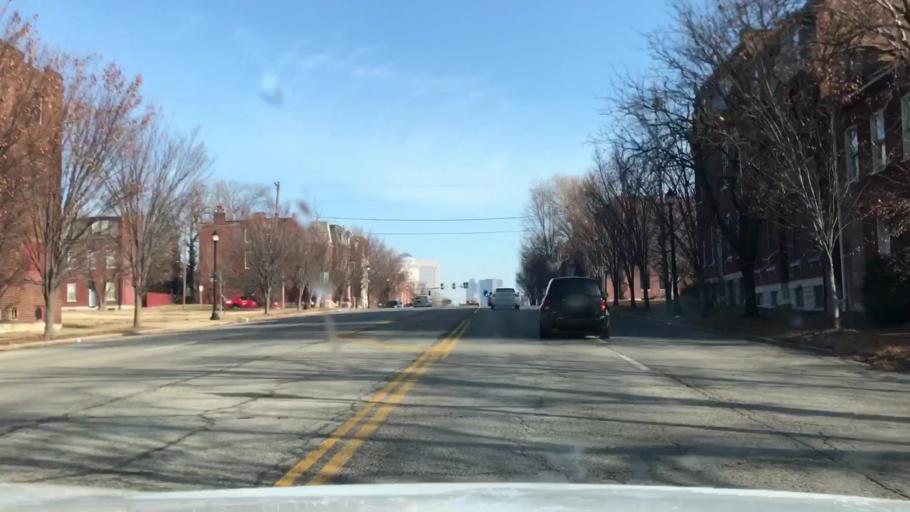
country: US
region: Missouri
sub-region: City of Saint Louis
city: St. Louis
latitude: 38.6113
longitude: -90.2075
